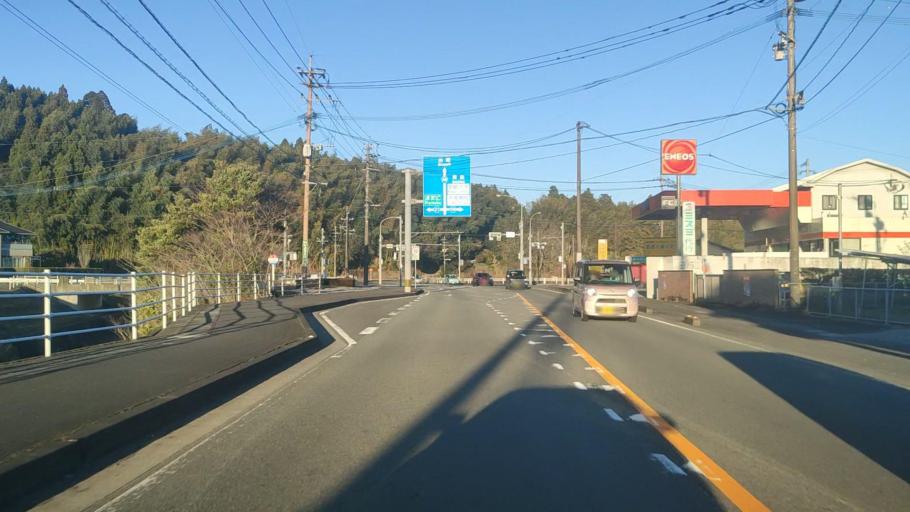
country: JP
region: Miyazaki
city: Miyazaki-shi
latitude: 31.8582
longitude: 131.3675
